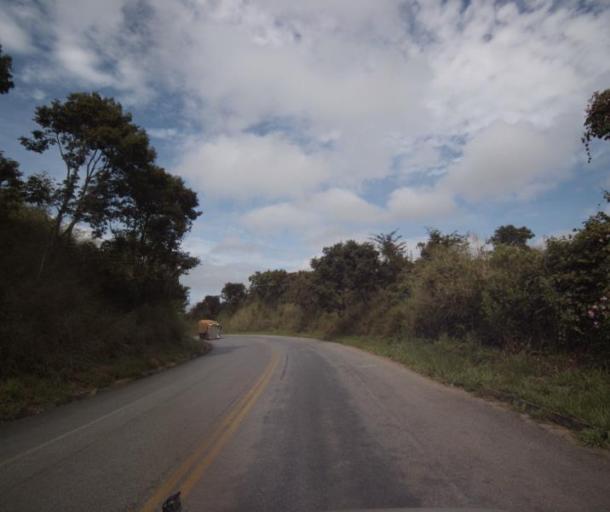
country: BR
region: Goias
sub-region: Pirenopolis
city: Pirenopolis
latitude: -15.7108
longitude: -48.6934
